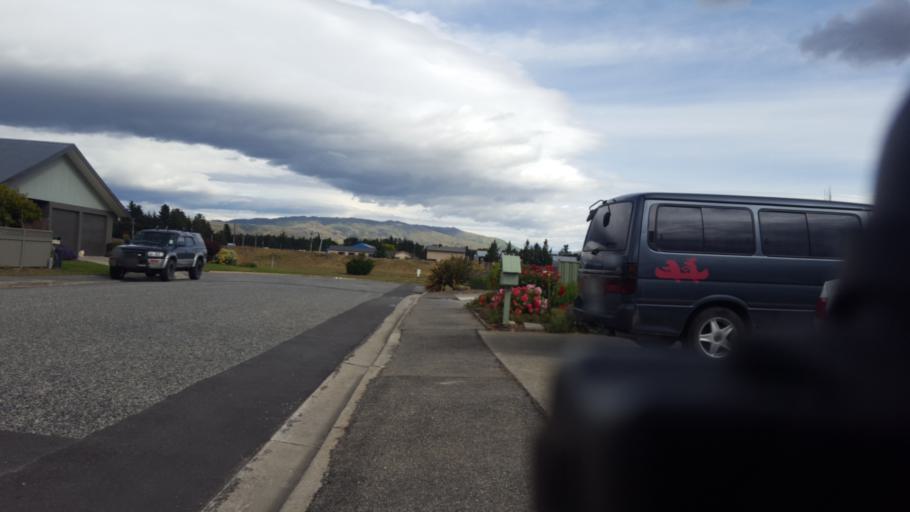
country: NZ
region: Otago
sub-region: Queenstown-Lakes District
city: Wanaka
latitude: -45.2407
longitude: 169.3915
